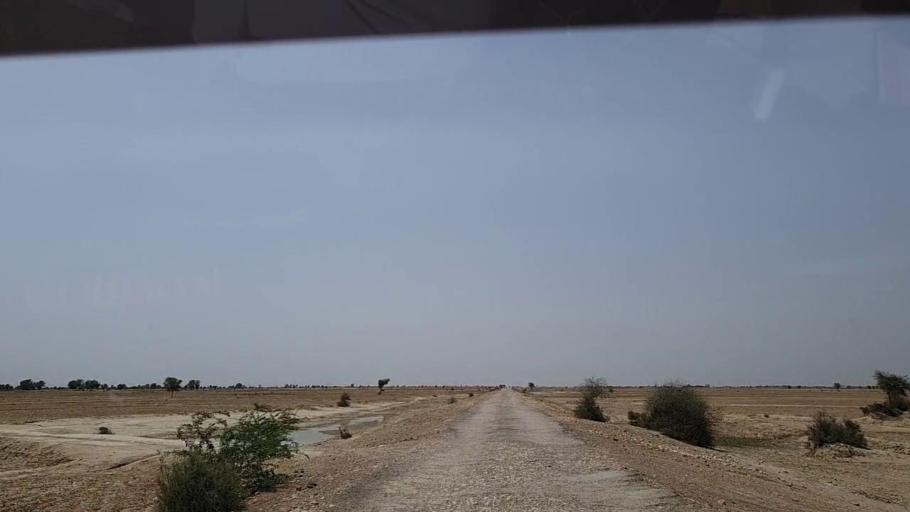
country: PK
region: Sindh
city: Johi
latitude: 26.7183
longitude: 67.6470
